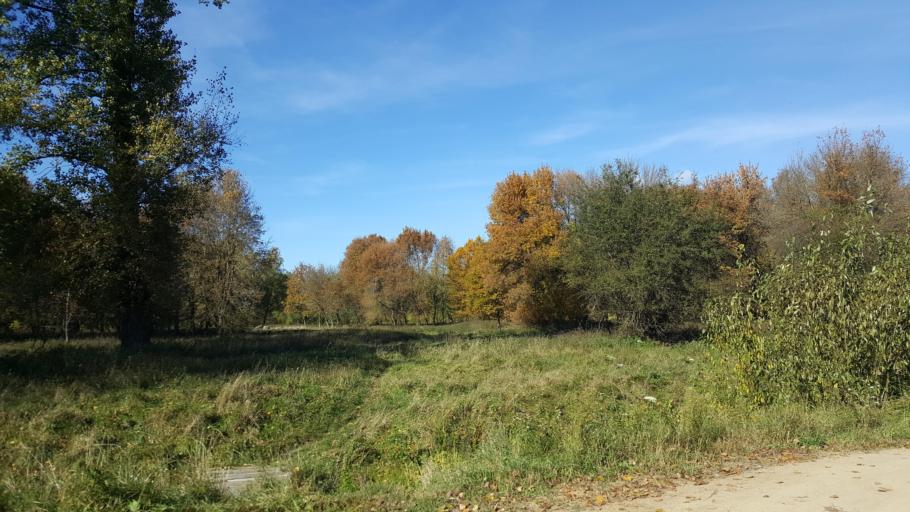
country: BY
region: Brest
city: Kamyanyets
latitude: 52.3971
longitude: 23.8085
